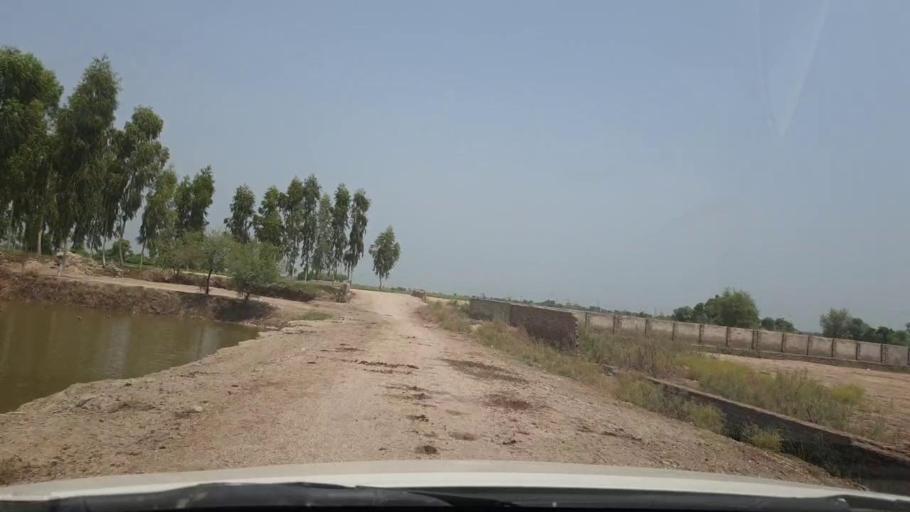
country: PK
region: Sindh
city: Rustam jo Goth
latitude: 28.0294
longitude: 68.7894
